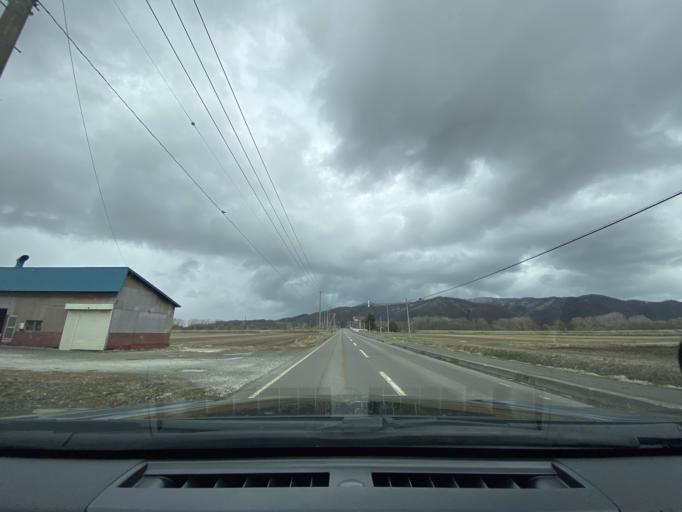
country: JP
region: Hokkaido
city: Nayoro
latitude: 44.1241
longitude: 142.4832
